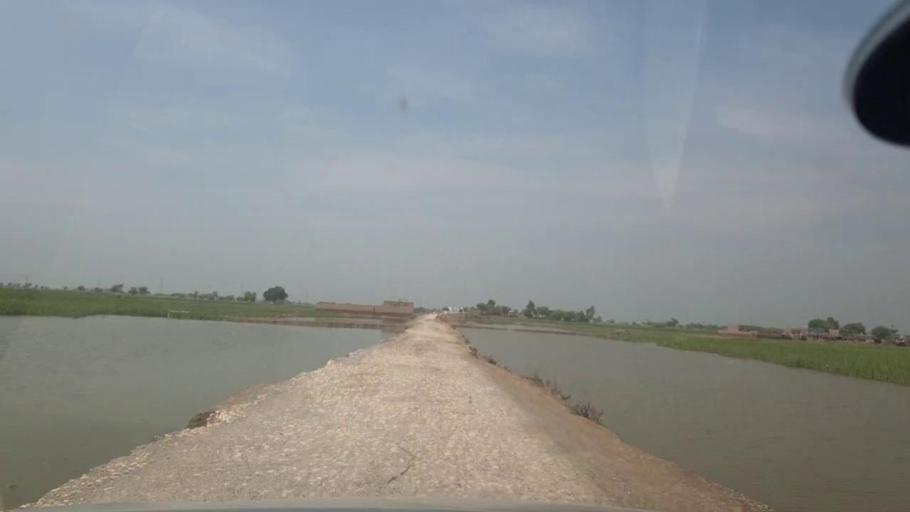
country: PK
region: Sindh
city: Thul
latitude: 28.1709
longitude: 68.6315
